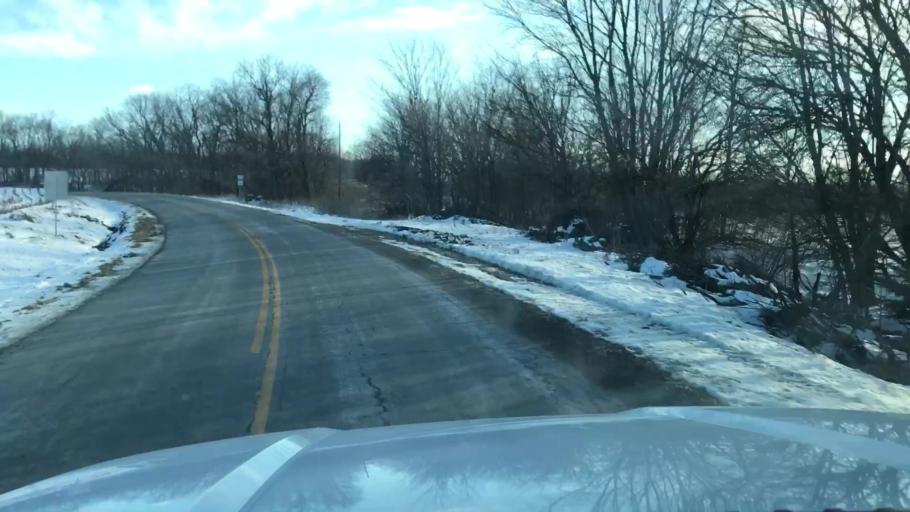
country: US
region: Missouri
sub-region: Holt County
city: Oregon
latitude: 40.1031
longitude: -95.0226
